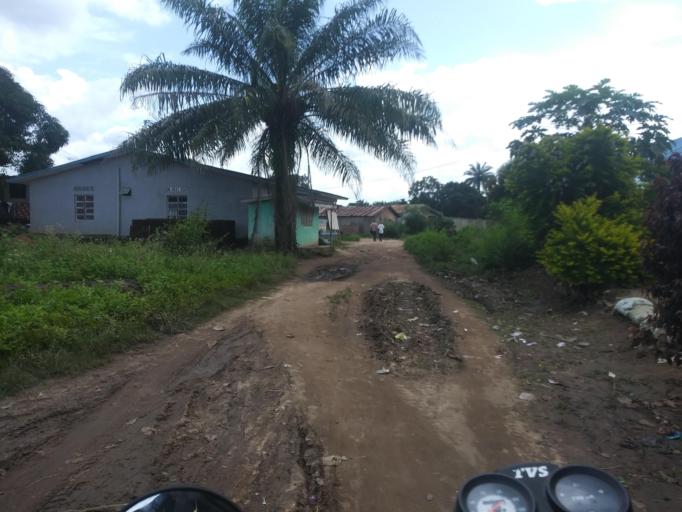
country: SL
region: Northern Province
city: Makeni
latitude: 8.8716
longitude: -12.0427
